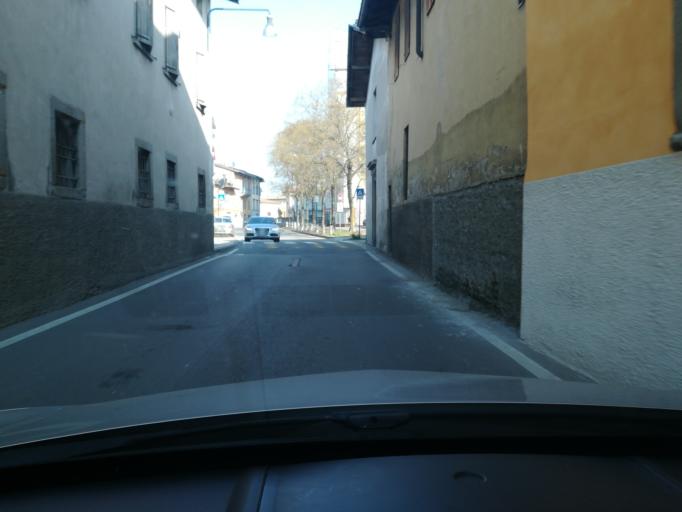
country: IT
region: Lombardy
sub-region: Provincia di Bergamo
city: Stezzano
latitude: 45.6495
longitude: 9.6524
